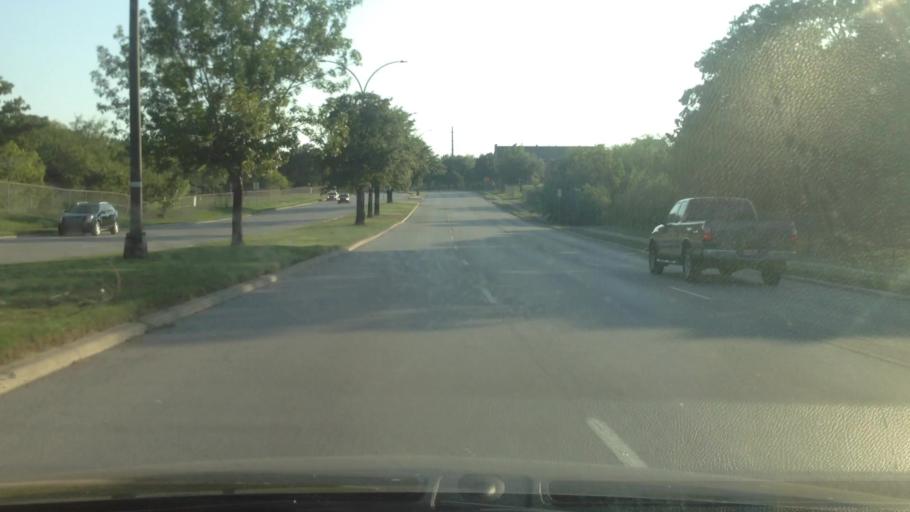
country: US
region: Texas
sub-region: Tarrant County
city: Pantego
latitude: 32.7139
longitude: -97.1869
